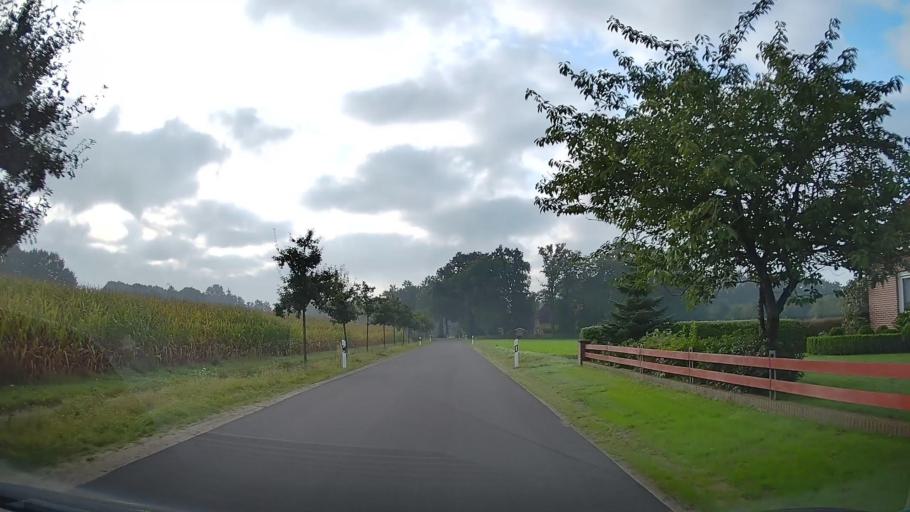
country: DE
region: Lower Saxony
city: Wardenburg
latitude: 53.0104
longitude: 8.1358
